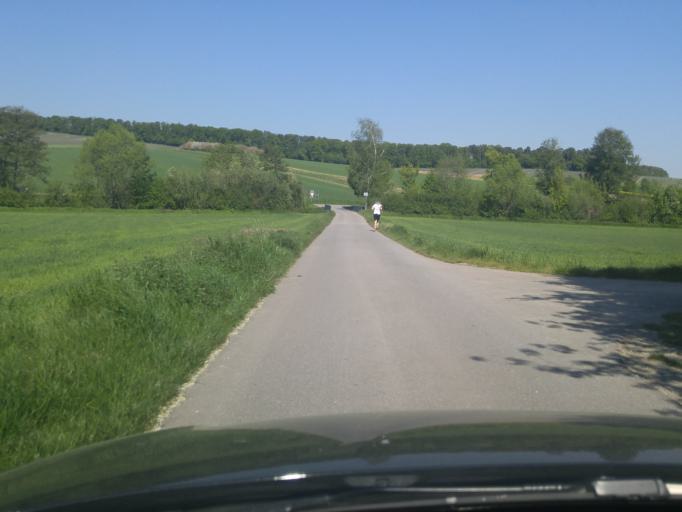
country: DE
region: Baden-Wuerttemberg
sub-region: Regierungsbezirk Stuttgart
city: Pfaffenhofen
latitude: 49.1040
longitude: 8.9795
